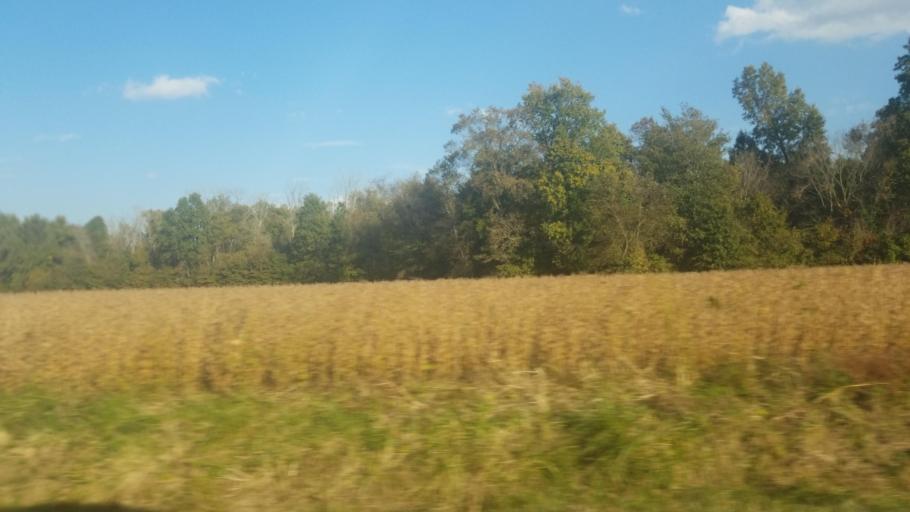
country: US
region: Illinois
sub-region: Saline County
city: Harrisburg
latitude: 37.8218
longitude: -88.6147
